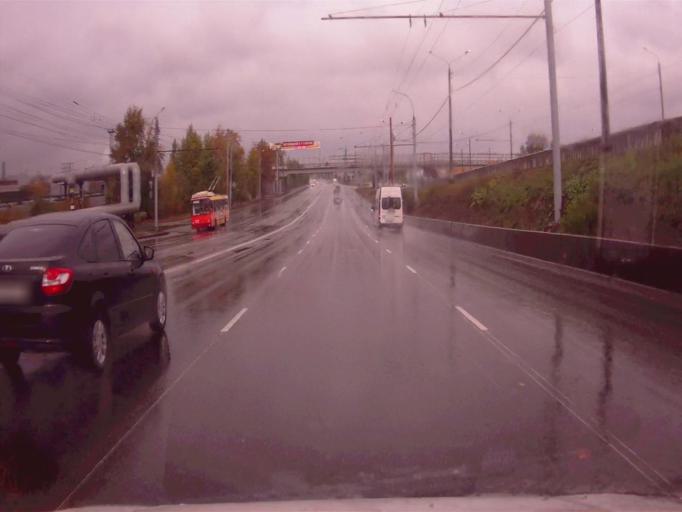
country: RU
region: Chelyabinsk
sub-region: Gorod Chelyabinsk
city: Chelyabinsk
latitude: 55.1992
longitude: 61.3859
